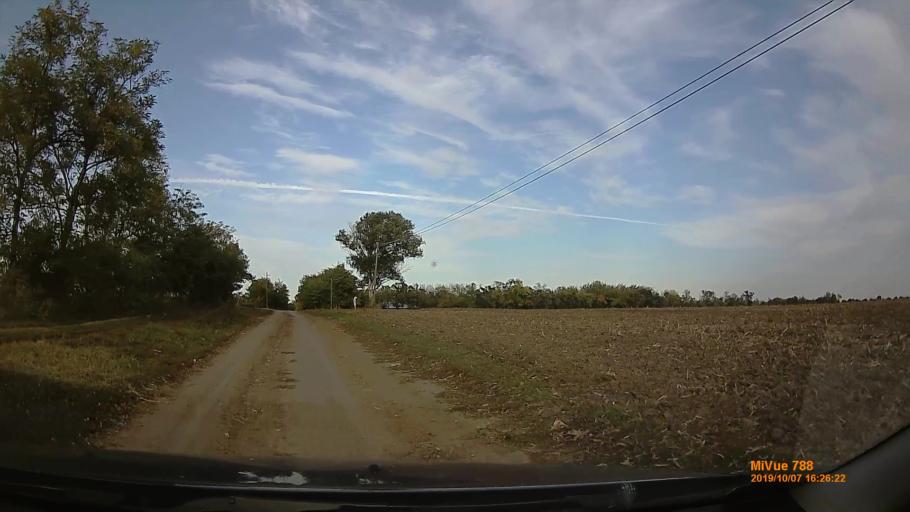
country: HU
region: Bekes
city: Szarvas
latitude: 46.8191
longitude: 20.6382
